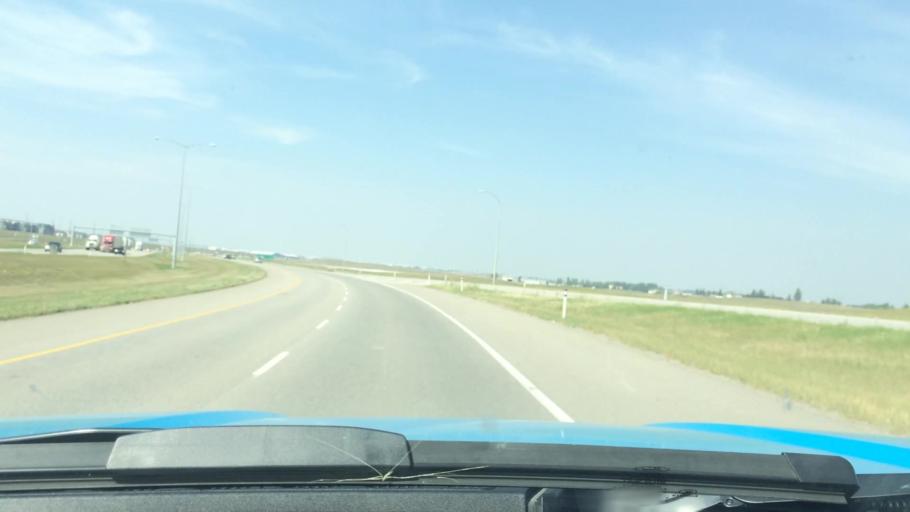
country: CA
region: Alberta
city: Chestermere
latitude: 50.9158
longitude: -113.9107
